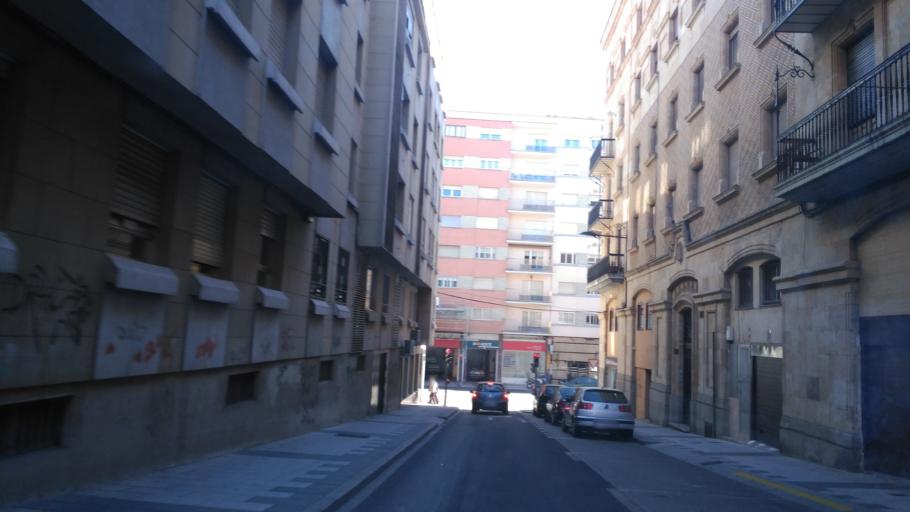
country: ES
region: Castille and Leon
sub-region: Provincia de Salamanca
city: Salamanca
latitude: 40.9708
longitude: -5.6534
